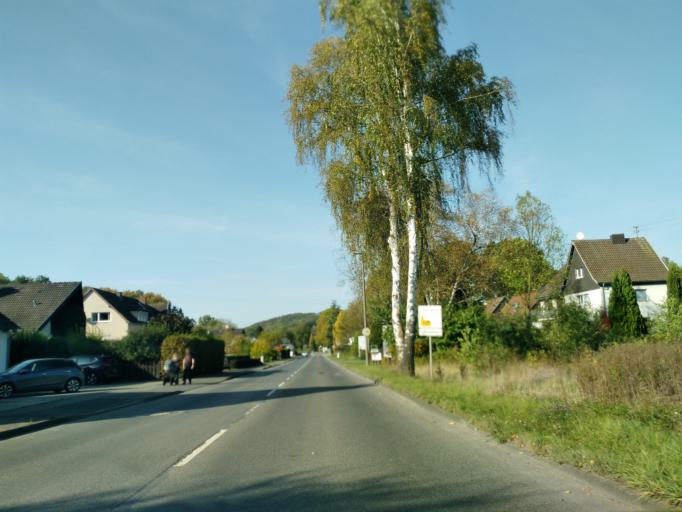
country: DE
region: North Rhine-Westphalia
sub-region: Regierungsbezirk Koln
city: Hennef
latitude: 50.7262
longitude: 7.2715
